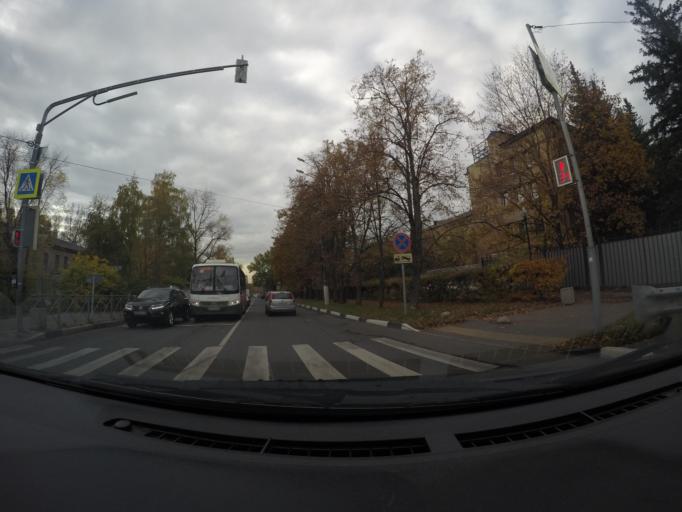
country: RU
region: Moskovskaya
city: Mytishchi
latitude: 55.9163
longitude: 37.7341
